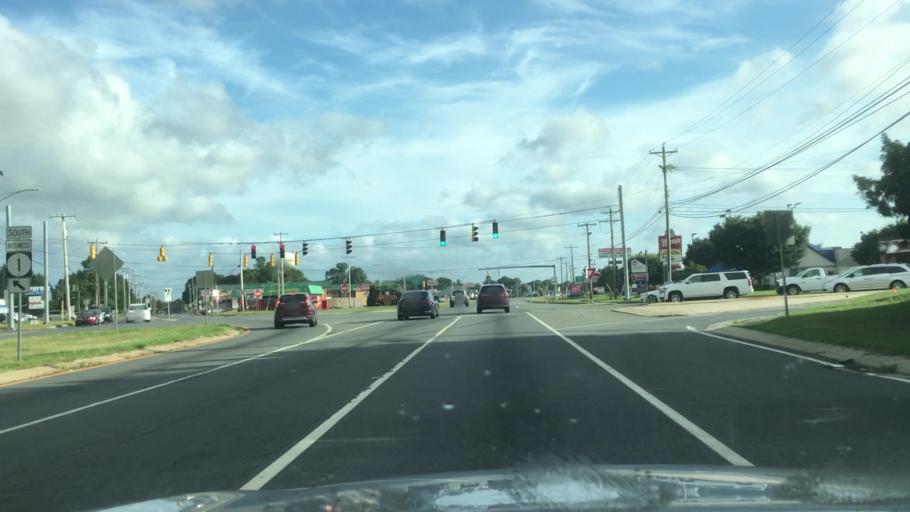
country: US
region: Delaware
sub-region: Sussex County
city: Milford
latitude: 38.9339
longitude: -75.4301
